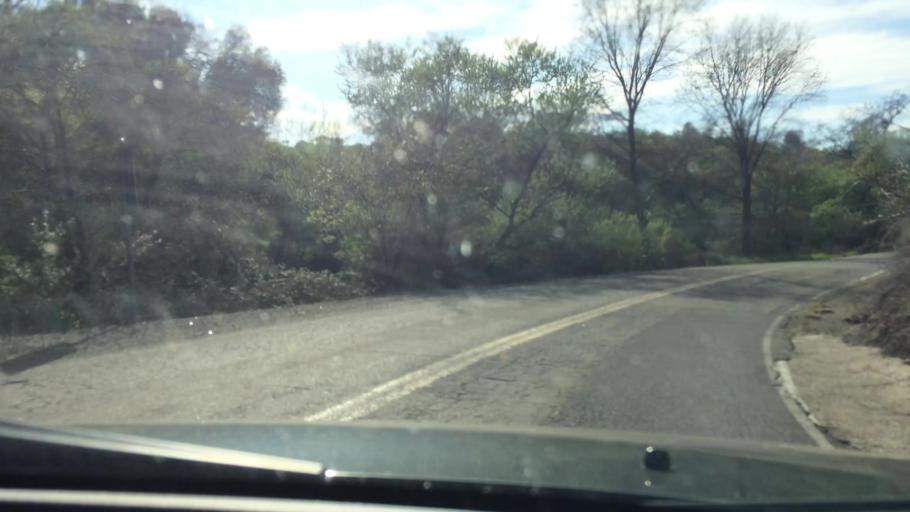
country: US
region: California
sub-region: Amador County
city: Plymouth
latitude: 38.4800
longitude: -120.8670
